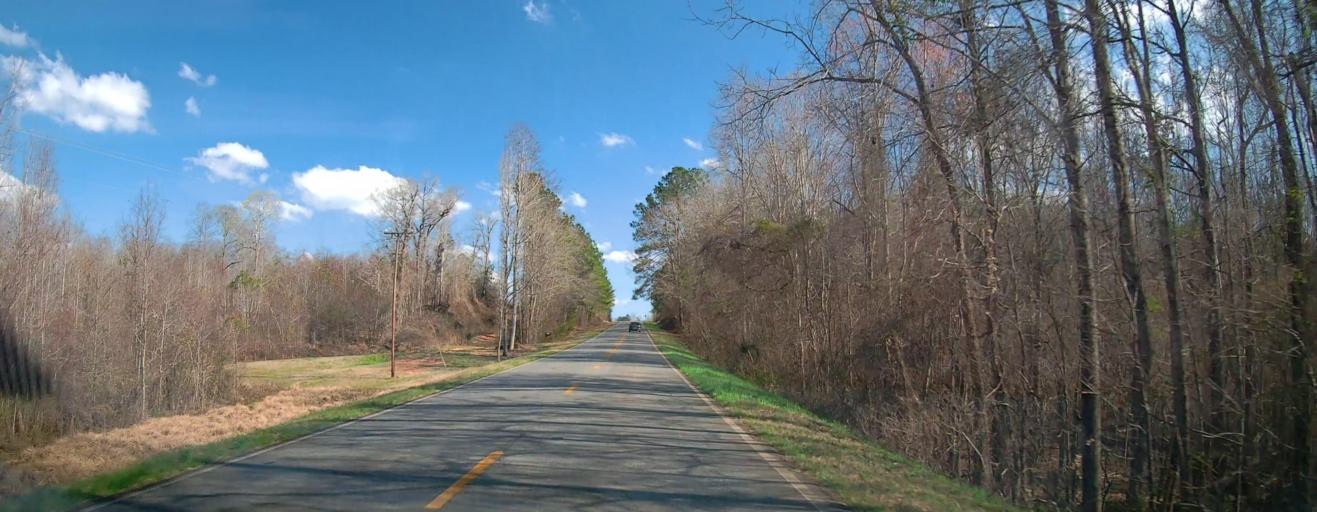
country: US
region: Georgia
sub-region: Laurens County
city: Dublin
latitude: 32.5731
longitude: -83.0446
